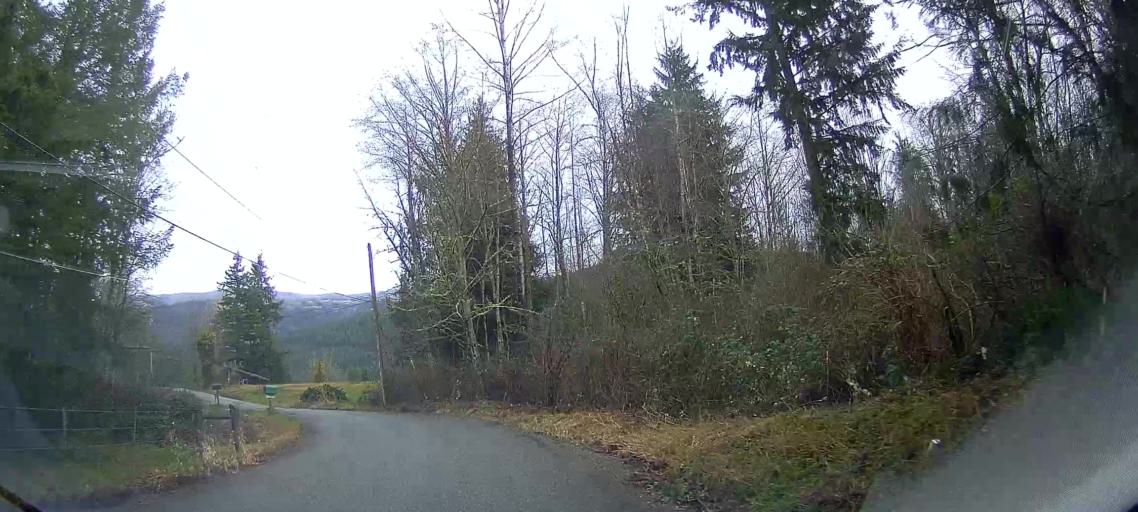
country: US
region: Washington
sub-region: Skagit County
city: Sedro-Woolley
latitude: 48.5904
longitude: -122.2247
